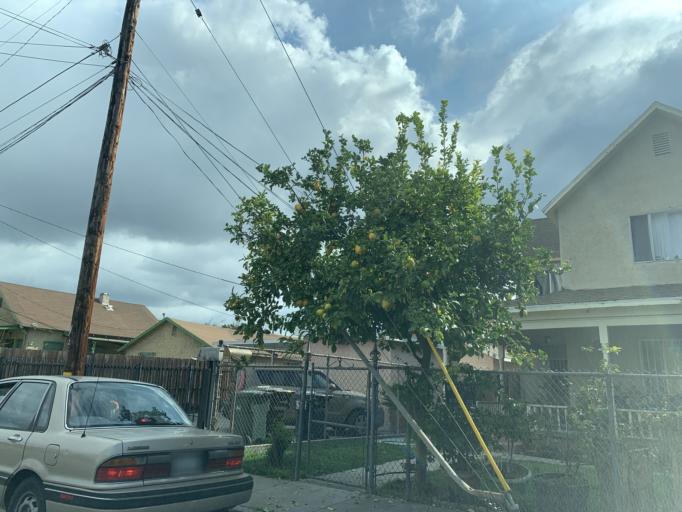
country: US
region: California
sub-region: Los Angeles County
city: Florence-Graham
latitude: 33.9813
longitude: -118.2432
